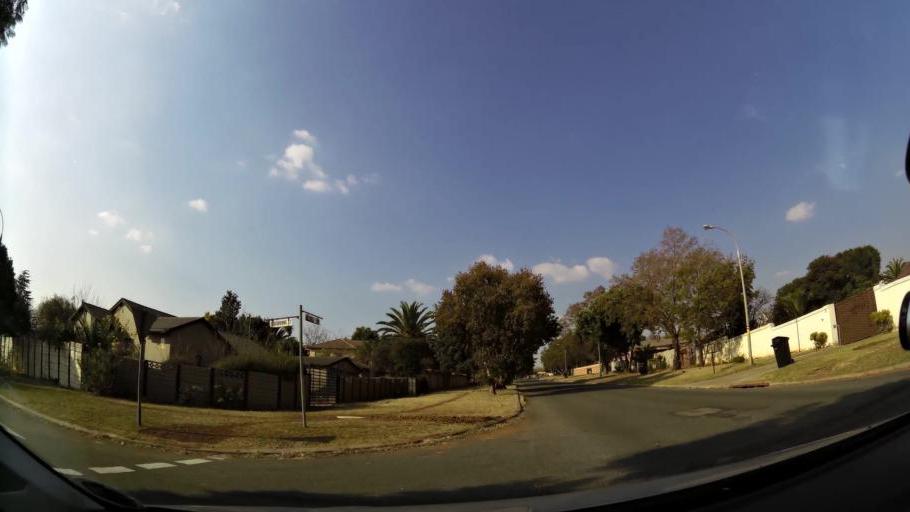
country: ZA
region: Gauteng
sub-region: City of Johannesburg Metropolitan Municipality
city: Modderfontein
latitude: -26.0990
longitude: 28.1893
